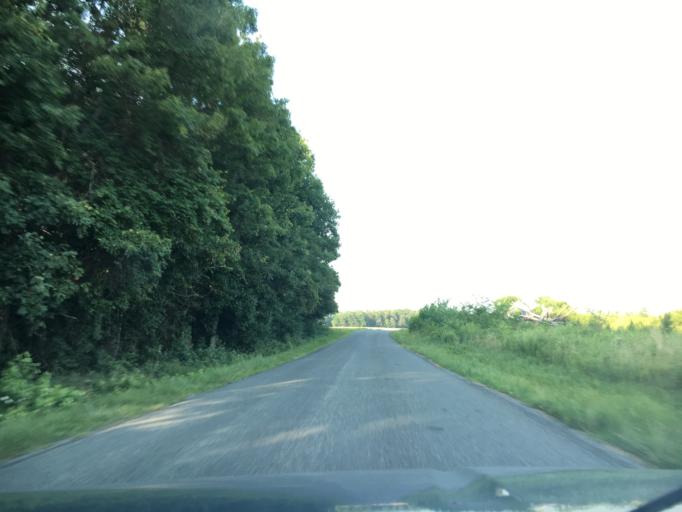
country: US
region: Virginia
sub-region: Halifax County
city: Mountain Road
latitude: 36.8433
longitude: -79.1566
